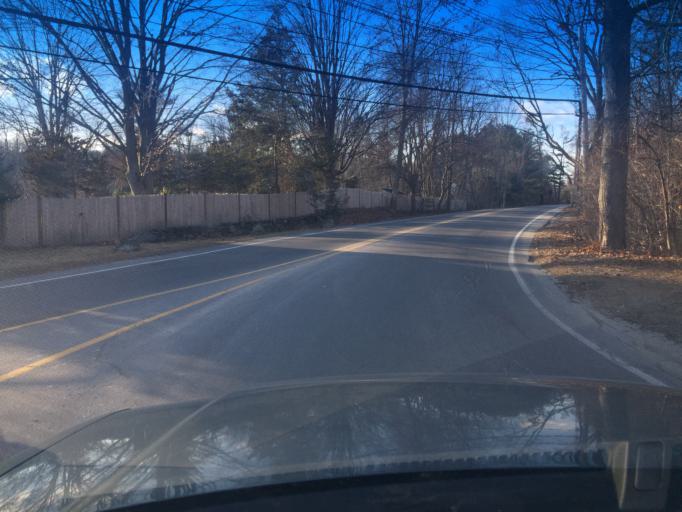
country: US
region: Massachusetts
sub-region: Middlesex County
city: Sherborn
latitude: 42.2559
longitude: -71.3686
